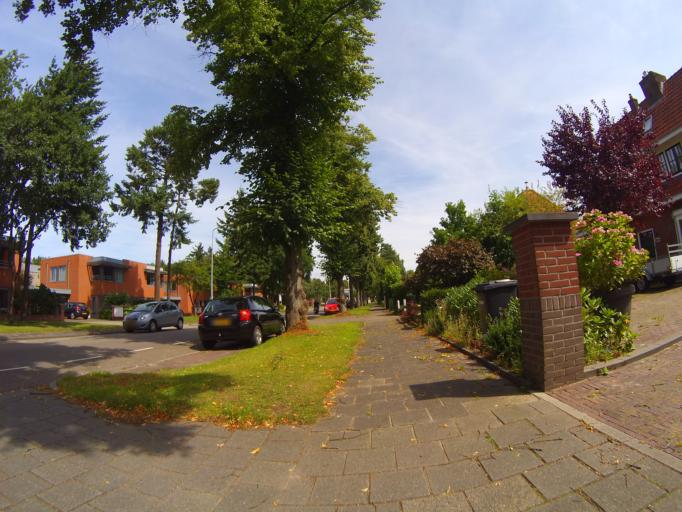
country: NL
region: Utrecht
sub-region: Gemeente Zeist
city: Zeist
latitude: 52.1011
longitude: 5.2541
